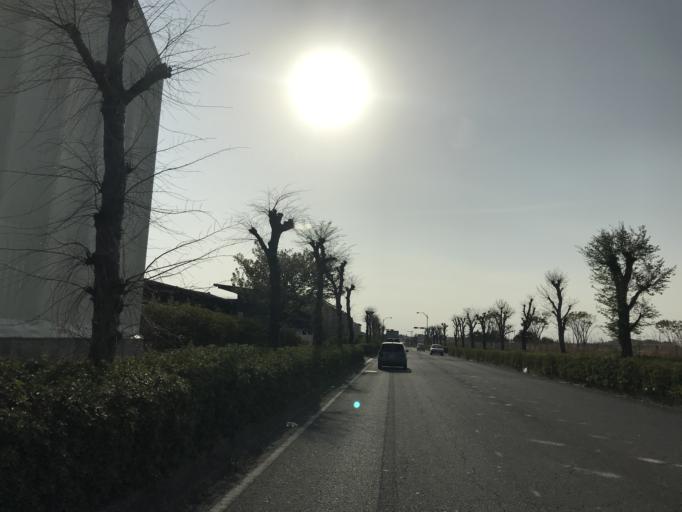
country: JP
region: Ibaraki
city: Hitachi-Naka
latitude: 36.4088
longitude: 140.5876
